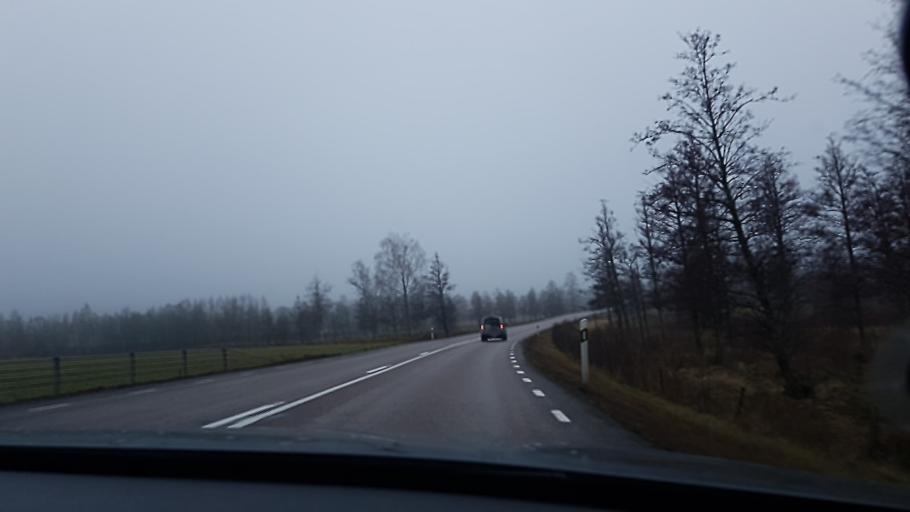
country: SE
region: Vaestra Goetaland
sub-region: Gullspangs Kommun
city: Gullspang
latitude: 58.9919
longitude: 14.1010
